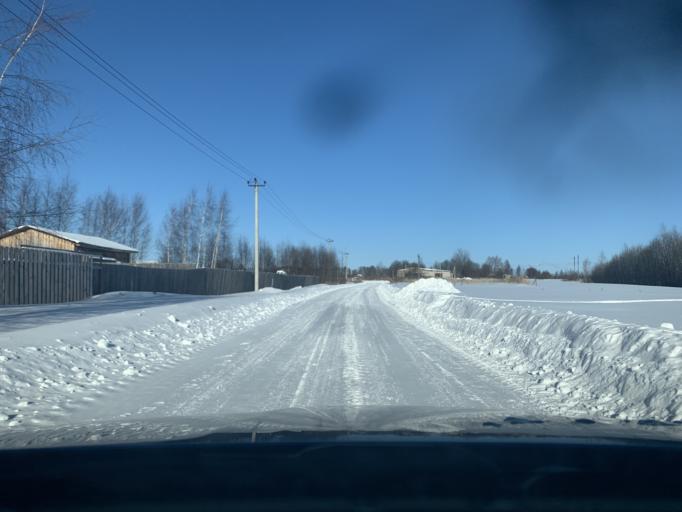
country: RU
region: Jaroslavl
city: Tunoshna
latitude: 57.6518
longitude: 40.0678
